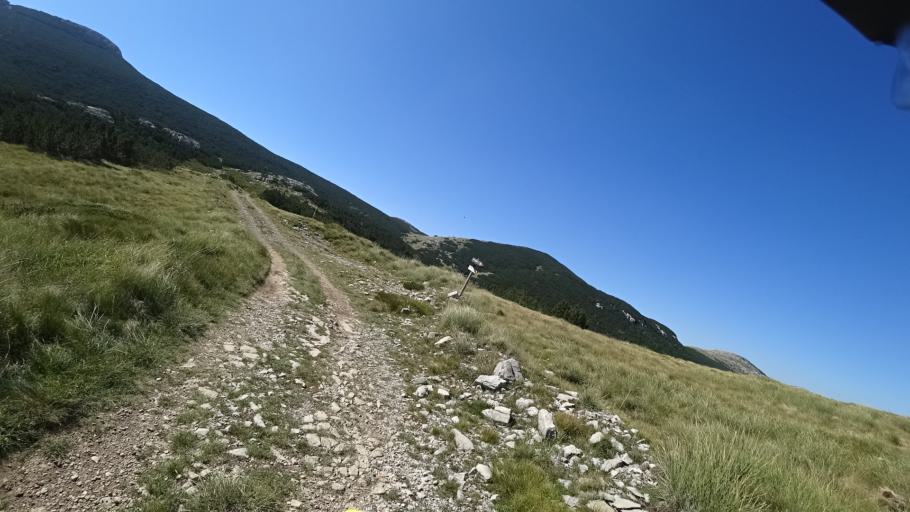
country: HR
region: Splitsko-Dalmatinska
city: Hrvace
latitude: 43.9409
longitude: 16.5814
